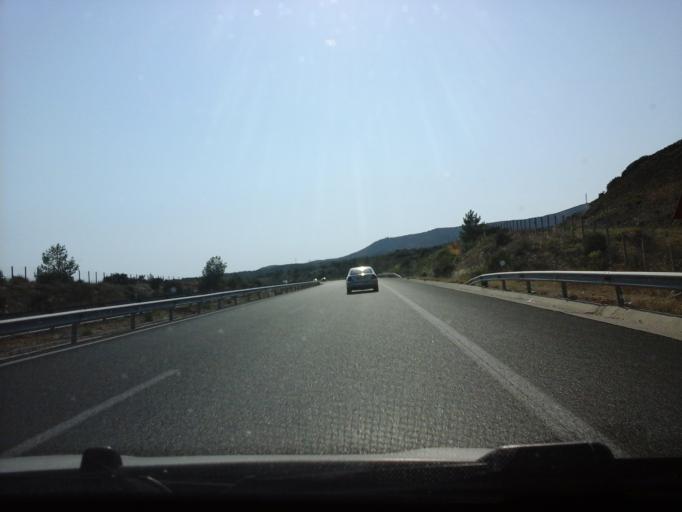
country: GR
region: East Macedonia and Thrace
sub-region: Nomos Evrou
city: Alexandroupoli
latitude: 40.8675
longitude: 25.7744
